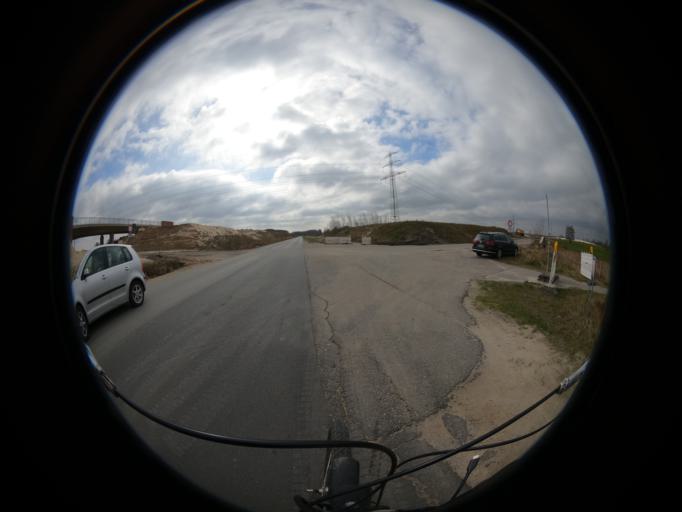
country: DE
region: Lower Saxony
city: Neu Wulmstorf
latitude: 53.4894
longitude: 9.7800
